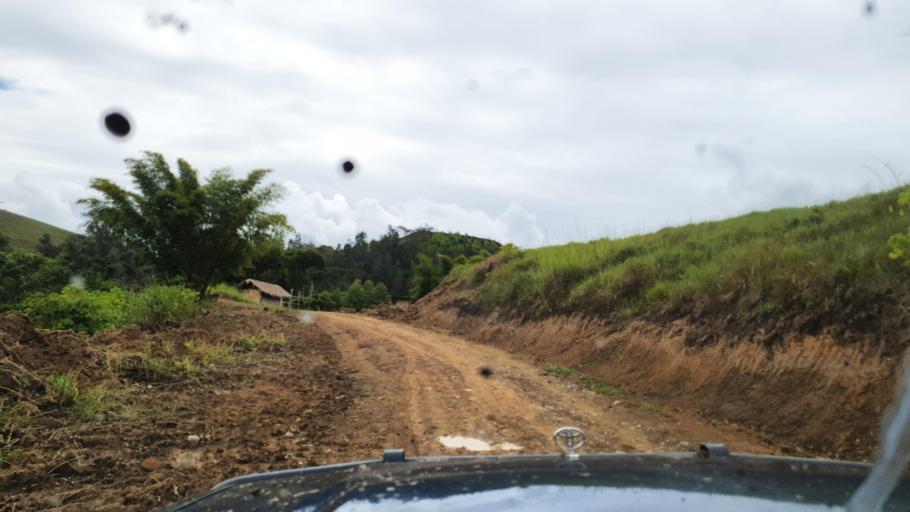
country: PG
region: Jiwaka
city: Minj
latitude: -5.9293
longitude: 144.7443
